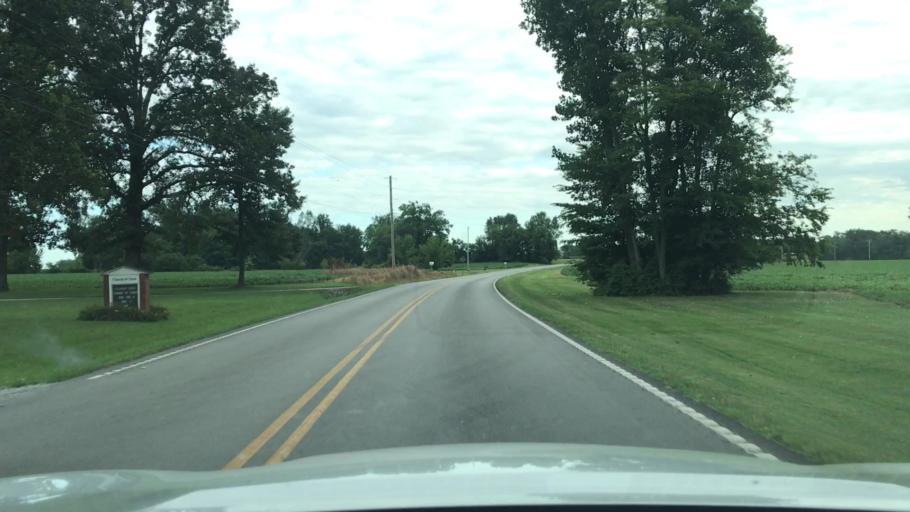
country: US
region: Kentucky
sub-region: Todd County
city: Guthrie
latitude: 36.7290
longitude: -87.1896
